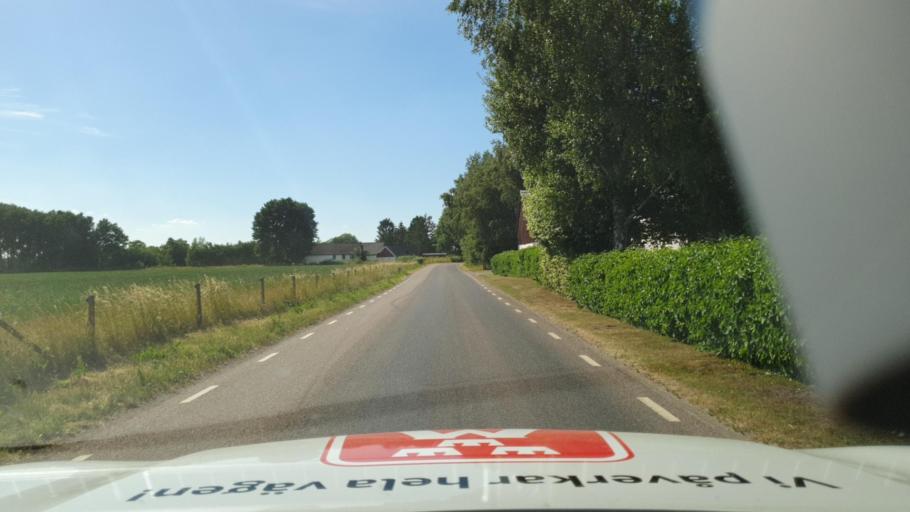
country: SE
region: Skane
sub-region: Sjobo Kommun
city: Blentarp
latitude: 55.6199
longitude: 13.6341
